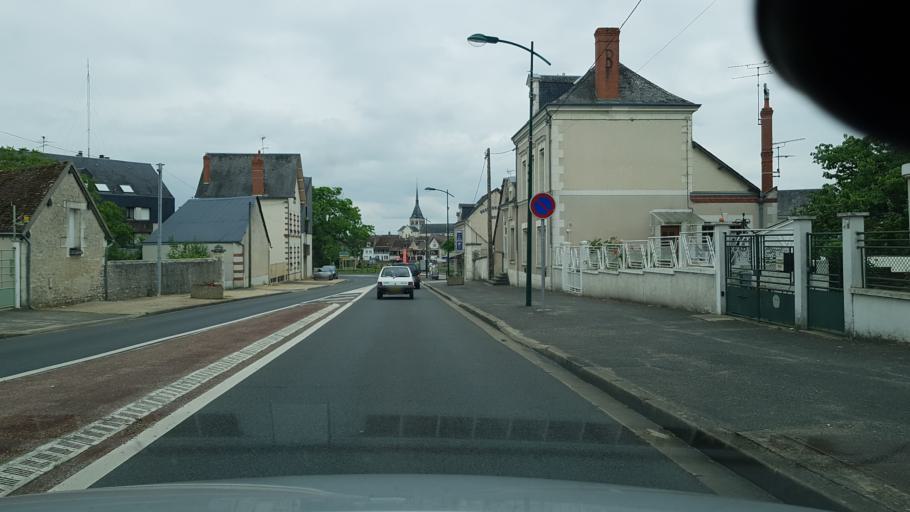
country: FR
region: Centre
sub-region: Departement du Loir-et-Cher
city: Selles-sur-Cher
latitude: 47.2786
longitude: 1.5492
